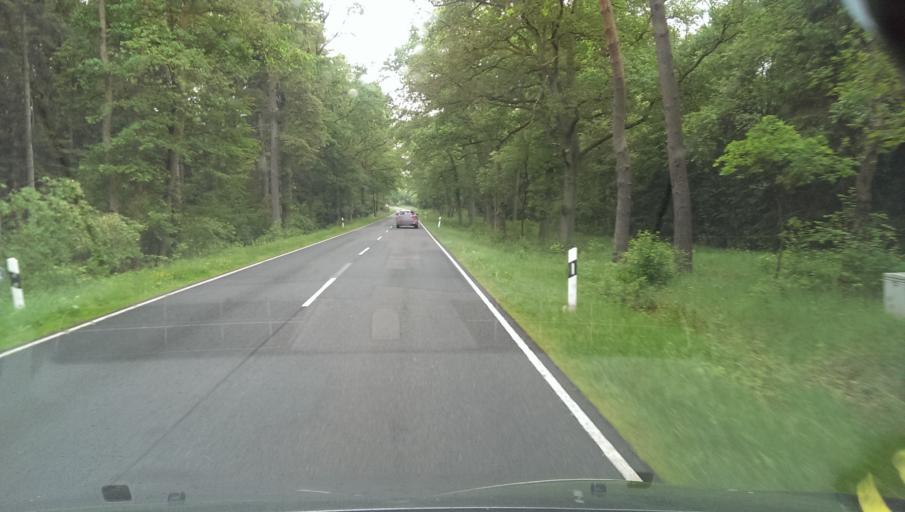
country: DE
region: Lower Saxony
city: Unterluss
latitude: 52.8672
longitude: 10.2515
